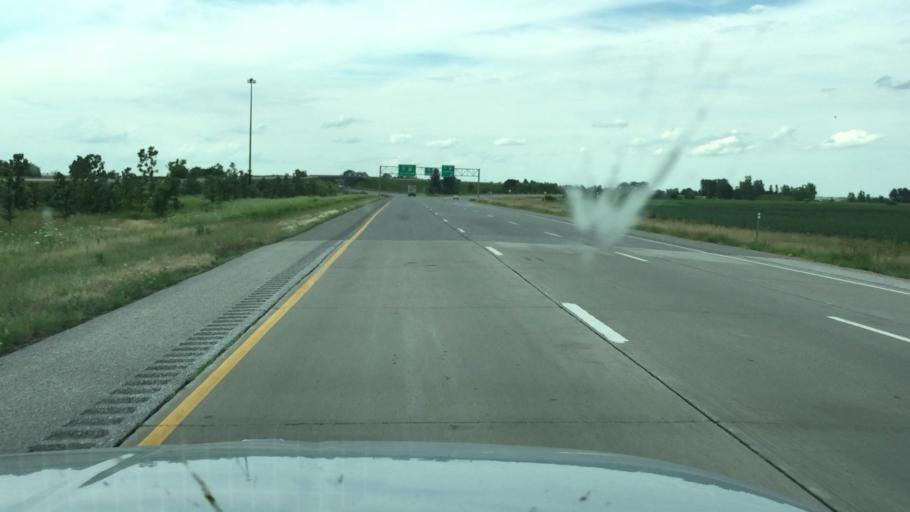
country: US
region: Iowa
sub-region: Scott County
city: Walcott
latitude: 41.5957
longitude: -90.6758
